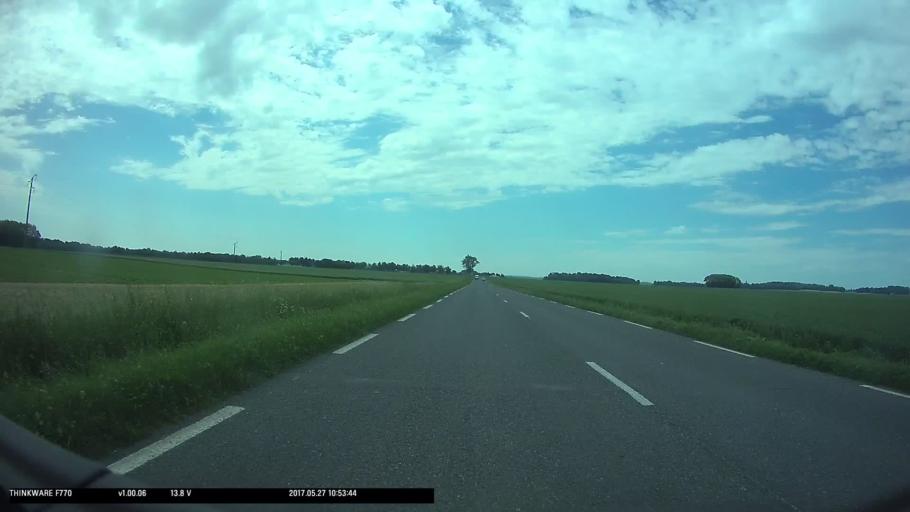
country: FR
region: Picardie
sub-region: Departement de l'Oise
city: Chaumont-en-Vexin
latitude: 49.2080
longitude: 1.8811
